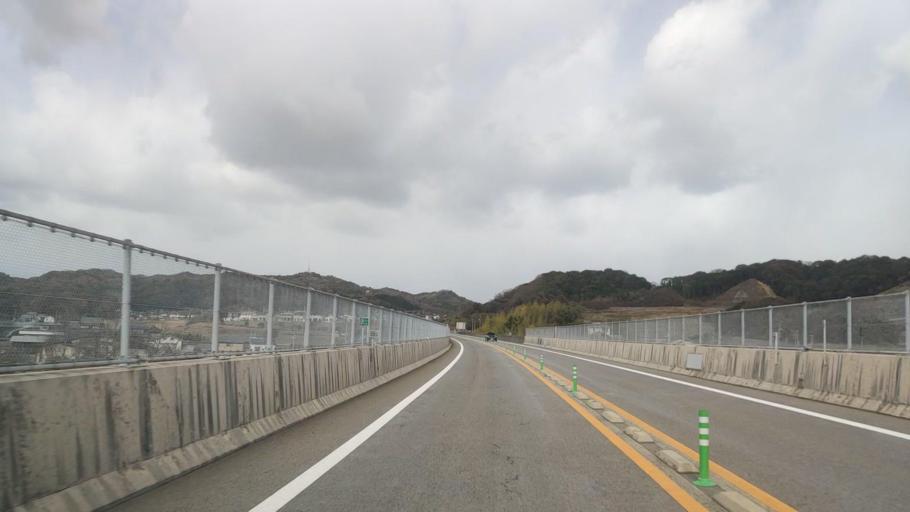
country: JP
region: Ehime
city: Hojo
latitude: 34.0623
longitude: 132.9729
